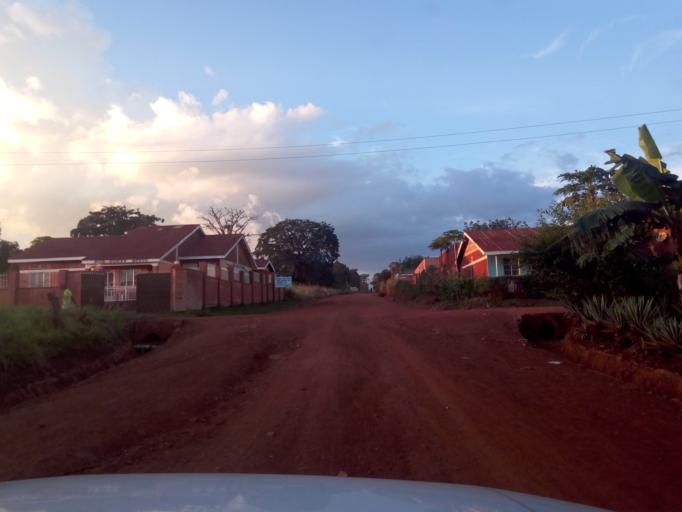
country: UG
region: Western Region
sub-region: Masindi District
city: Masindi
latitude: 1.6820
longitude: 31.7159
